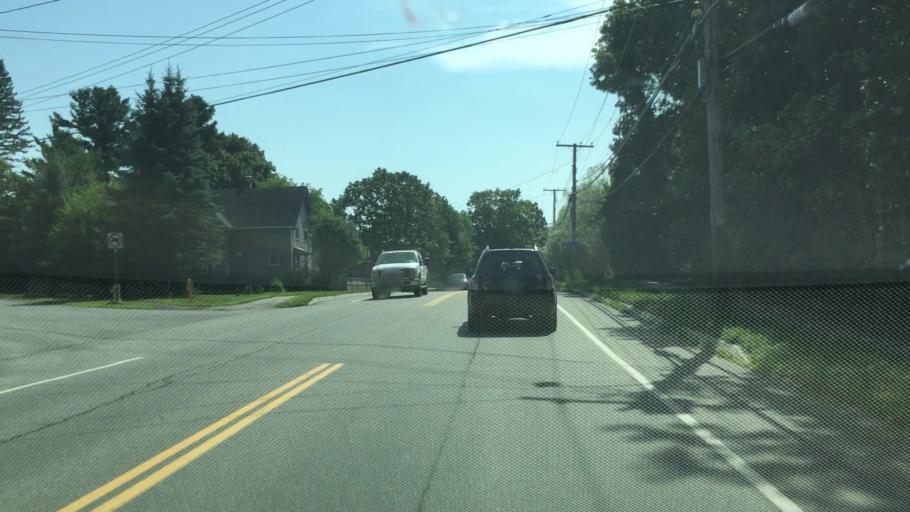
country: US
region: Maine
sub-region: Penobscot County
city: Brewer
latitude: 44.8165
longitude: -68.7648
